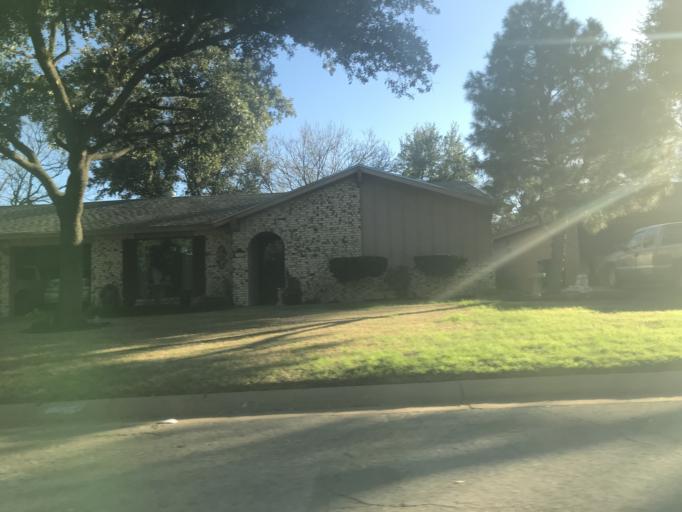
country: US
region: Texas
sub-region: Tom Green County
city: San Angelo
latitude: 31.4310
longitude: -100.4930
